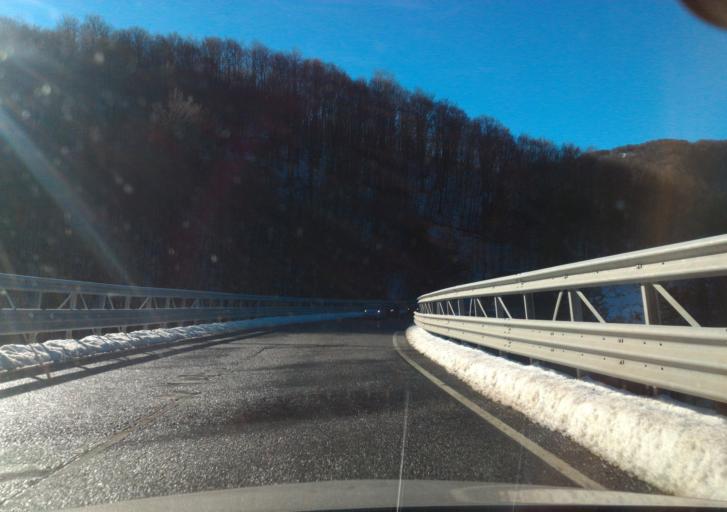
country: IT
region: Calabria
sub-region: Provincia di Cosenza
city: Celico
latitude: 39.3404
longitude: 16.3859
